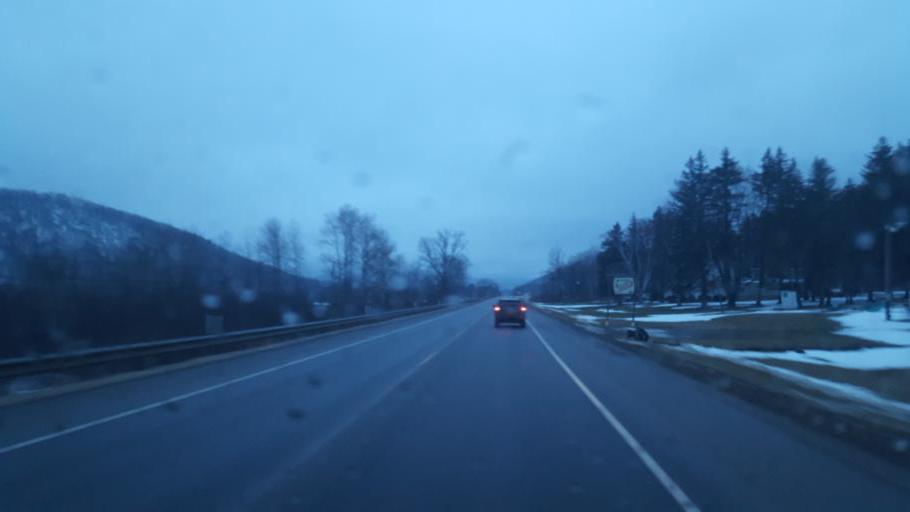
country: US
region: Pennsylvania
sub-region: McKean County
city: Port Allegany
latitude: 41.7910
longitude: -78.2412
